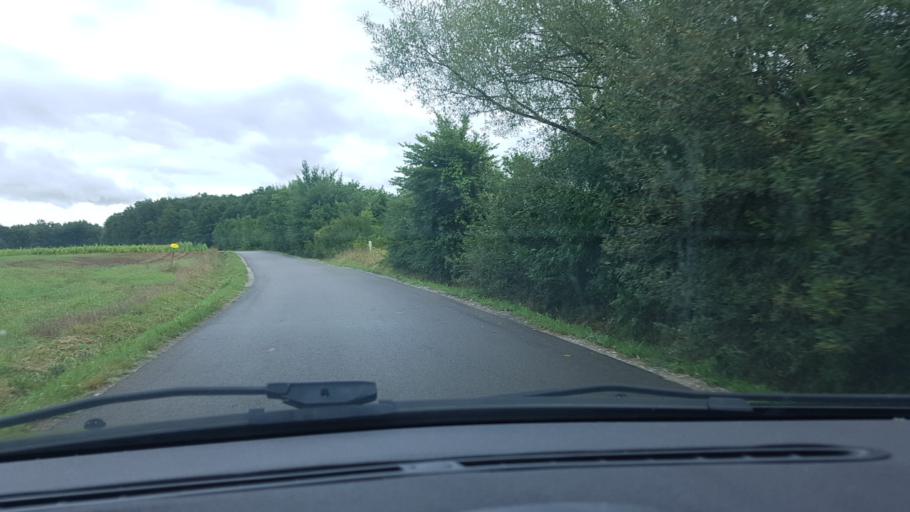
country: HR
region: Karlovacka
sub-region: Grad Karlovac
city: Karlovac
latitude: 45.5601
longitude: 15.5434
